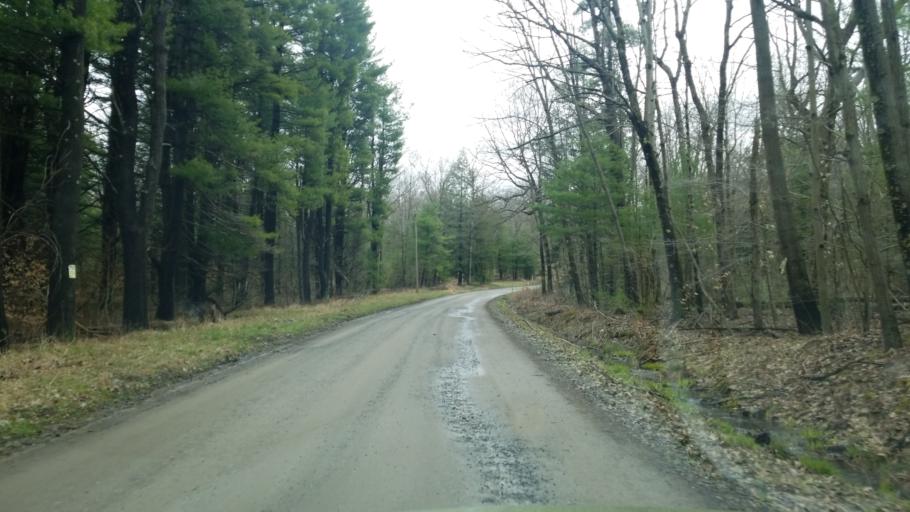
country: US
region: Pennsylvania
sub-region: Clearfield County
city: Shiloh
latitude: 41.1819
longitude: -78.3426
